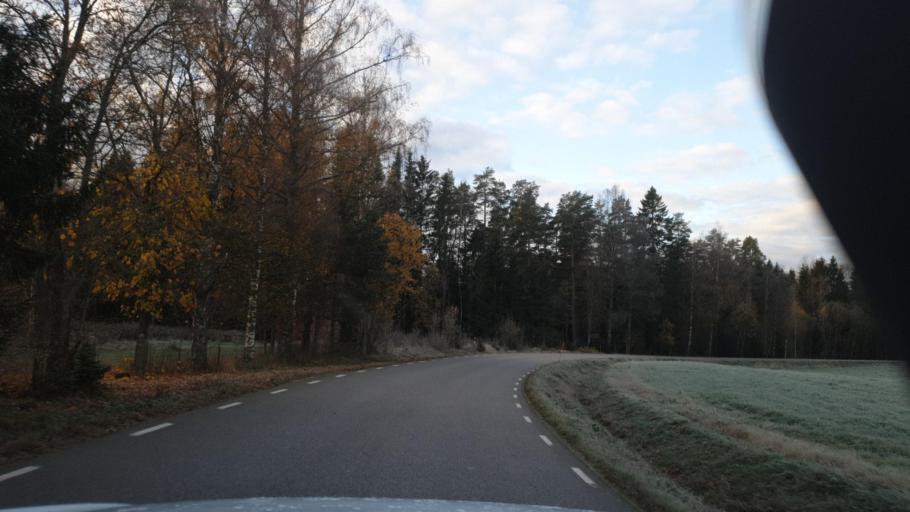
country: SE
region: Vaermland
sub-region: Eda Kommun
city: Amotfors
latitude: 59.7254
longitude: 12.1679
